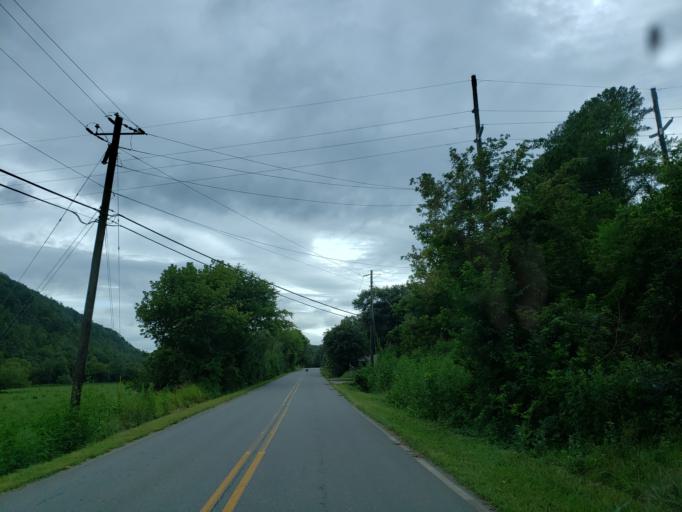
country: US
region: Georgia
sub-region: Pickens County
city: Jasper
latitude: 34.5653
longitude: -84.5115
